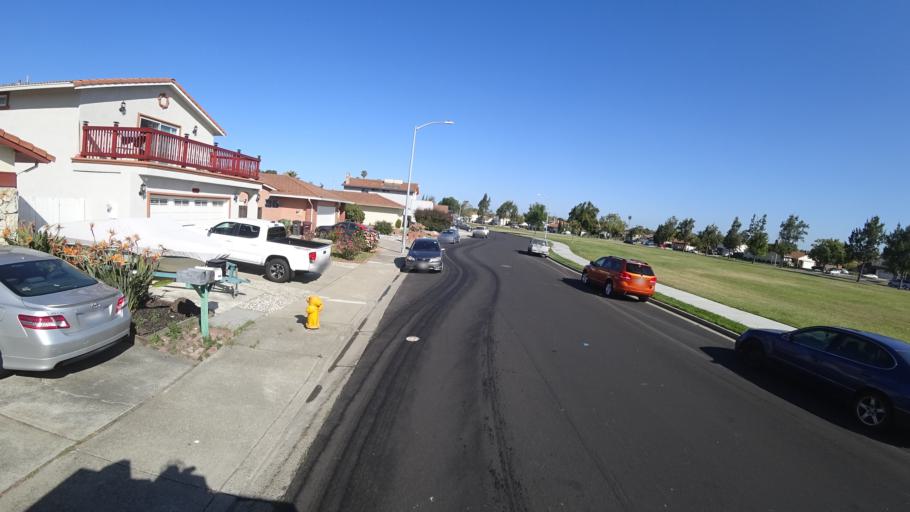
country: US
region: California
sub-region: Alameda County
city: Hayward
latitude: 37.6196
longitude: -122.0938
